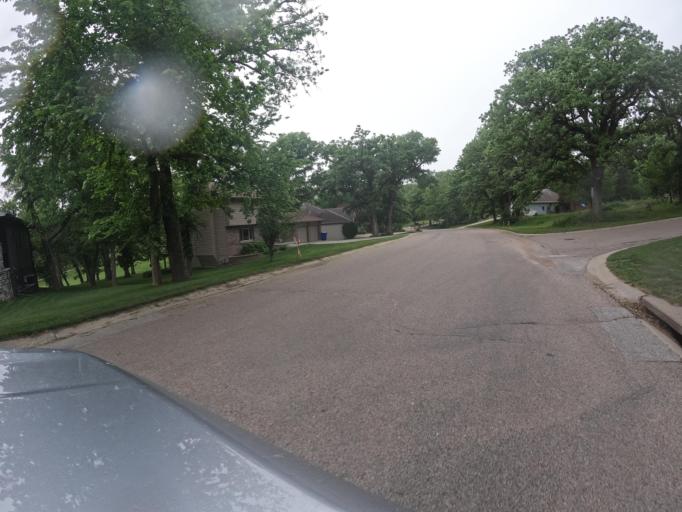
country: US
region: Nebraska
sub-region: Sarpy County
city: Offutt Air Force Base
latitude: 41.0509
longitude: -95.9671
